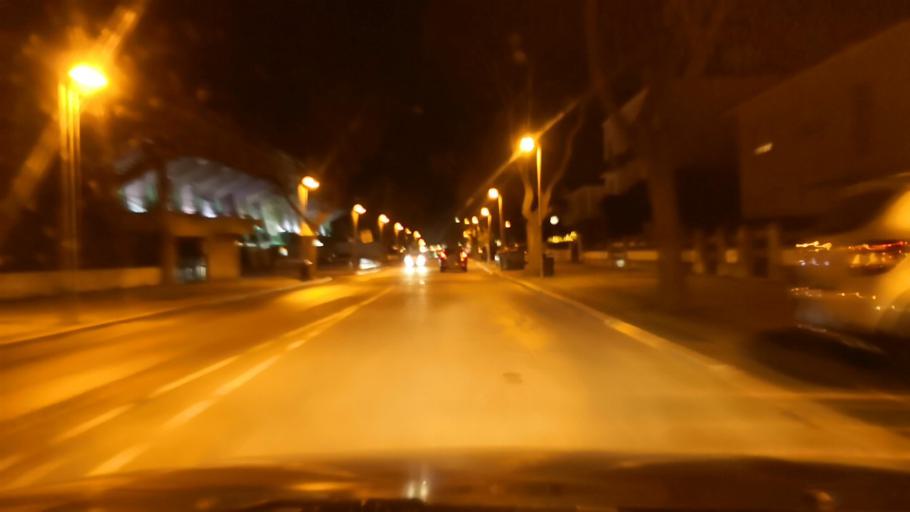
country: PT
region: Setubal
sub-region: Setubal
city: Setubal
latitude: 38.5319
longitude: -8.8924
